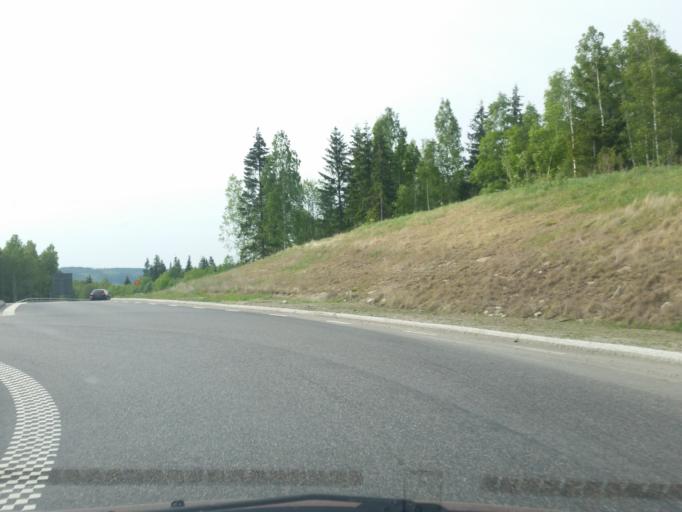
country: SE
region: Vaestra Goetaland
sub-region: Ulricehamns Kommun
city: Ulricehamn
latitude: 57.8070
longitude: 13.4535
